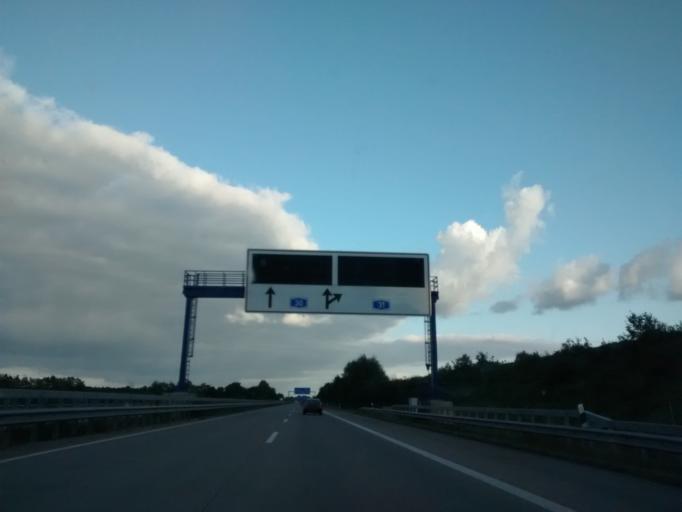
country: DE
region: Lower Saxony
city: Schuttorf
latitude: 52.3431
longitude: 7.2256
